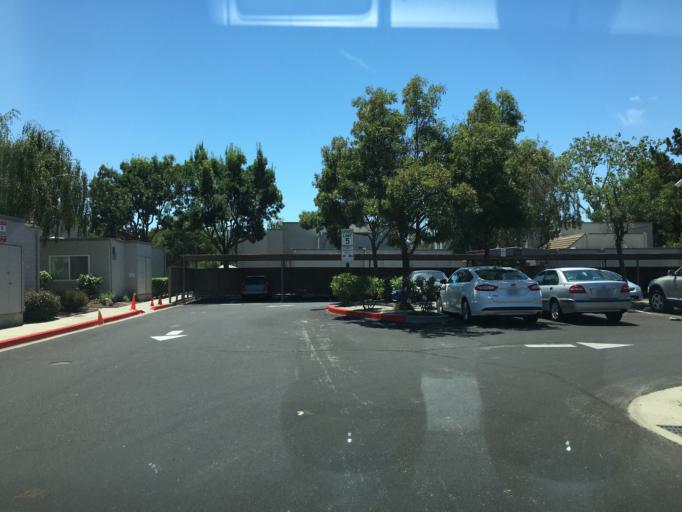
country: US
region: California
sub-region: San Mateo County
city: Redwood Shores
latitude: 37.5267
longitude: -122.2533
